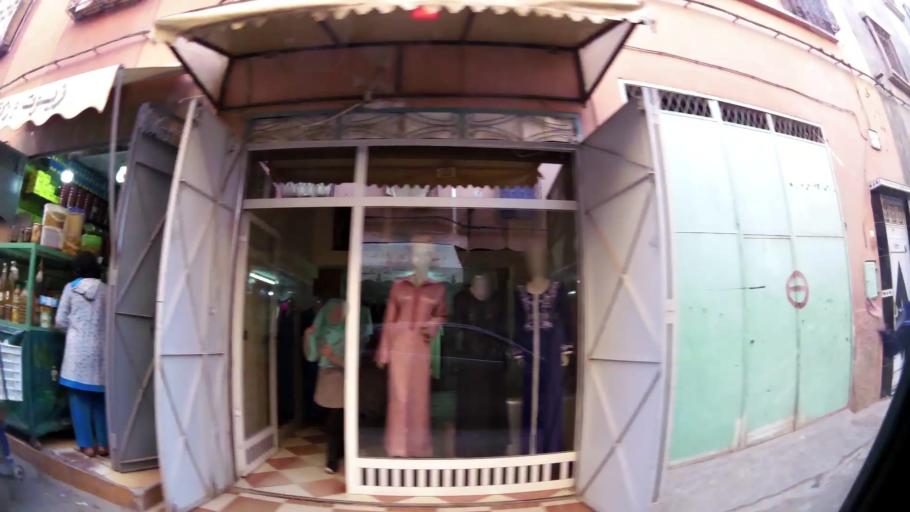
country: MA
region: Marrakech-Tensift-Al Haouz
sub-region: Marrakech
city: Marrakesh
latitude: 31.6104
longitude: -7.9636
